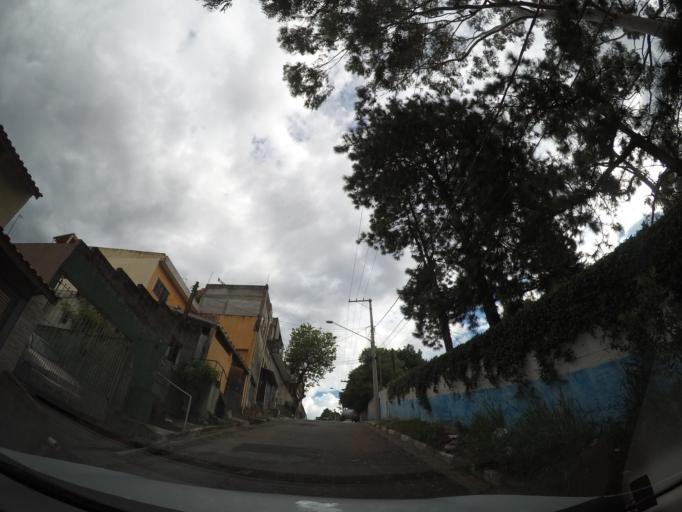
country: BR
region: Sao Paulo
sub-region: Guarulhos
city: Guarulhos
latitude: -23.4744
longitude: -46.5572
